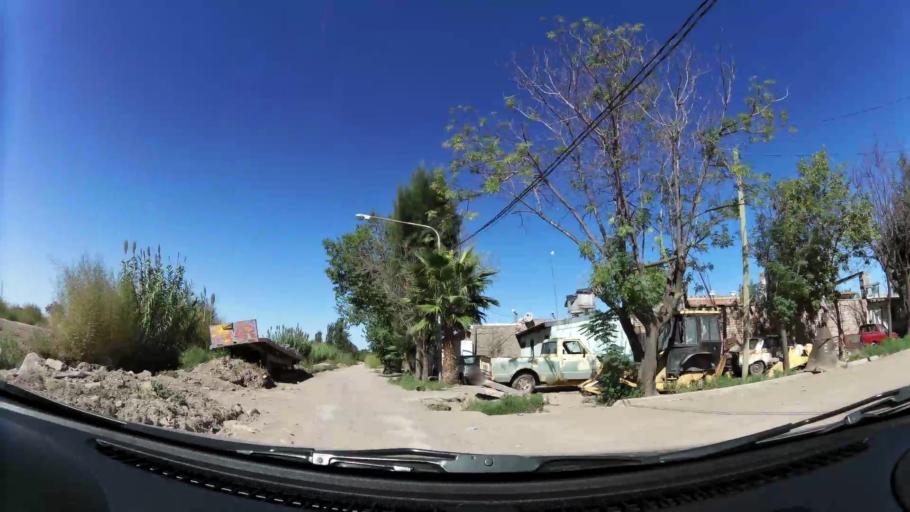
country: AR
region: Mendoza
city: Las Heras
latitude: -32.8248
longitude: -68.8136
